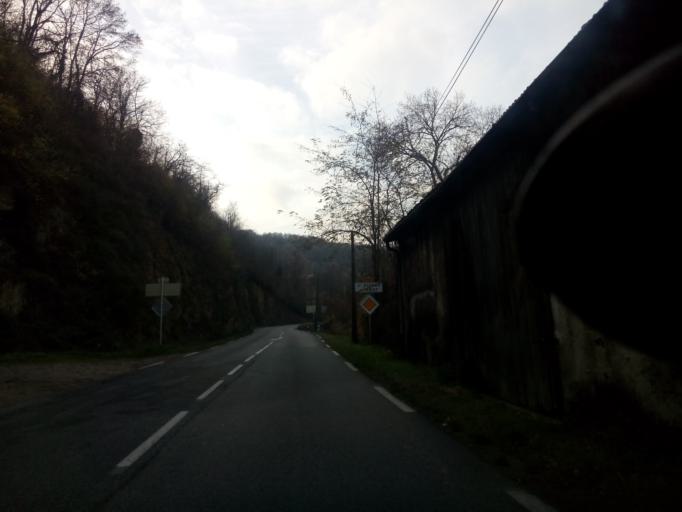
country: FR
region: Rhone-Alpes
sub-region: Departement de la Loire
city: Saint-Pierre-de-Boeuf
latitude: 45.3867
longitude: 4.7440
